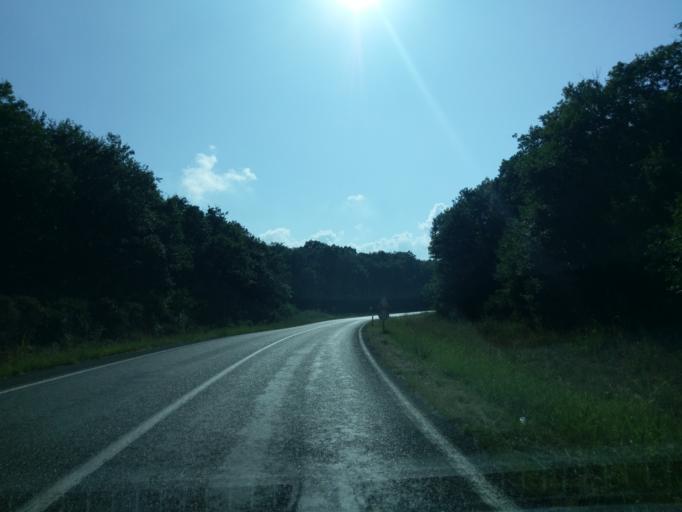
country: TR
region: Sinop
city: Yenikonak
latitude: 41.9447
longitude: 34.7414
